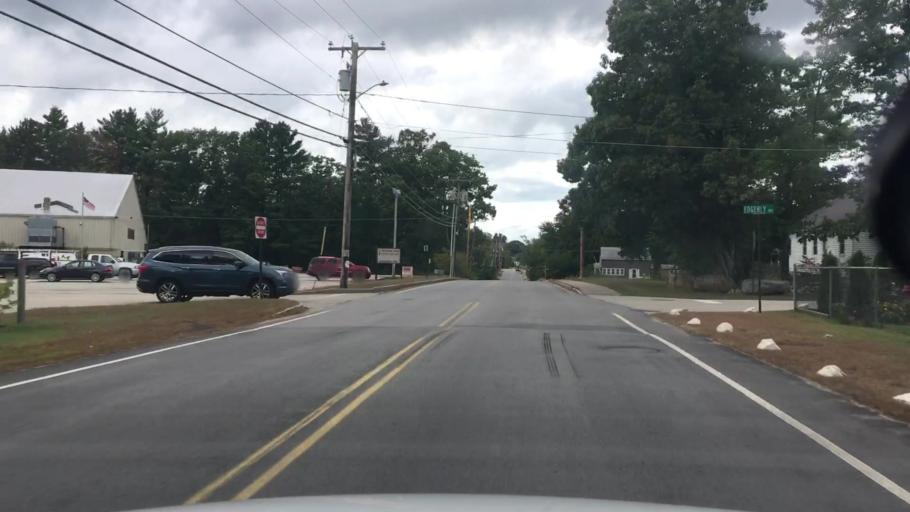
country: US
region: New Hampshire
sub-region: Strafford County
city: Rochester
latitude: 43.2909
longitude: -70.9687
